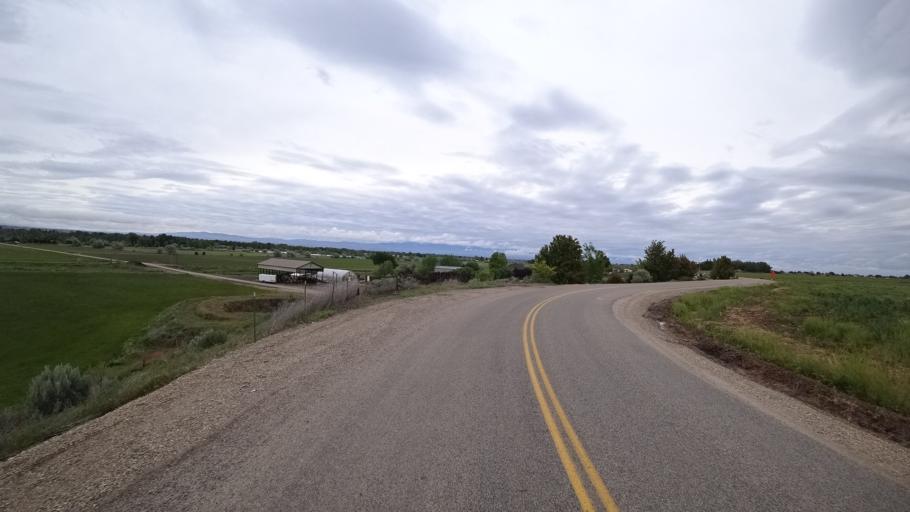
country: US
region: Idaho
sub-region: Ada County
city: Star
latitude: 43.6709
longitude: -116.5104
